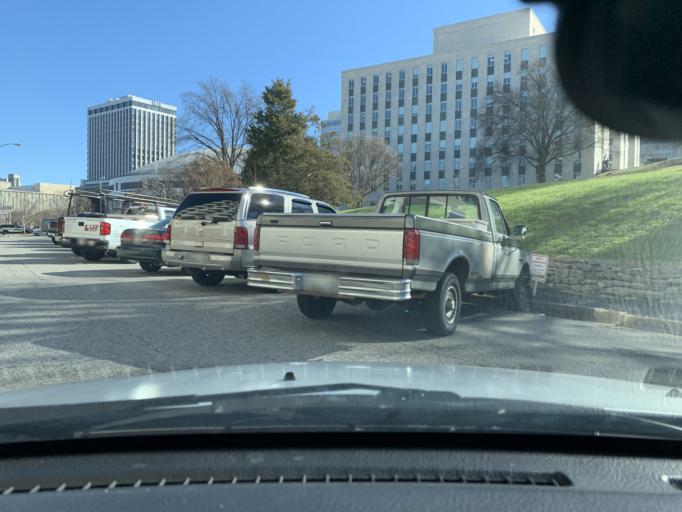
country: US
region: Tennessee
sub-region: Davidson County
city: Nashville
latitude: 36.1680
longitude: -86.7843
